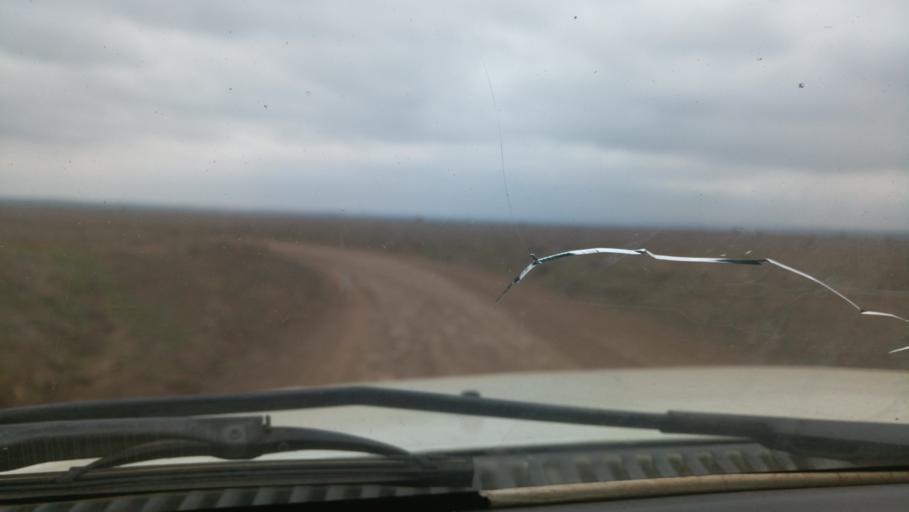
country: KE
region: Nairobi Area
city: Pumwani
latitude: -1.3560
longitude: 36.8579
